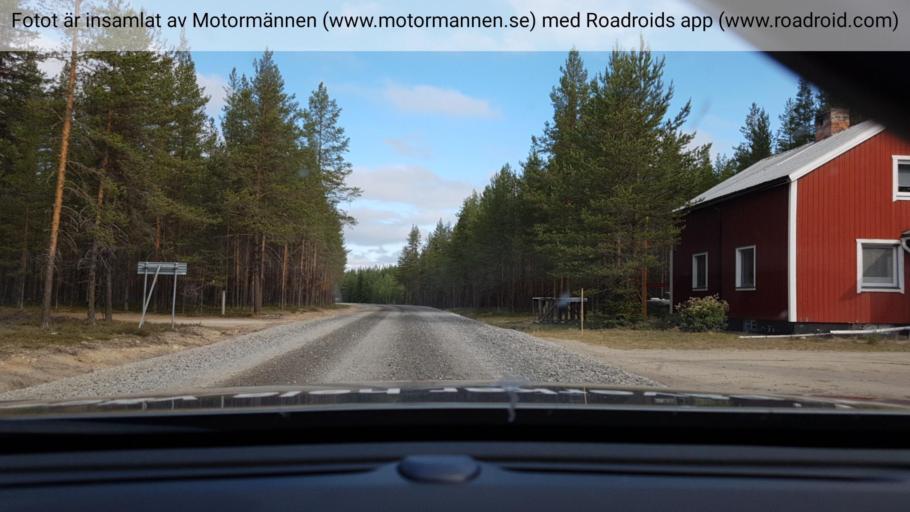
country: SE
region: Vaesterbotten
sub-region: Norsjo Kommun
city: Norsjoe
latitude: 64.6652
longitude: 19.2674
